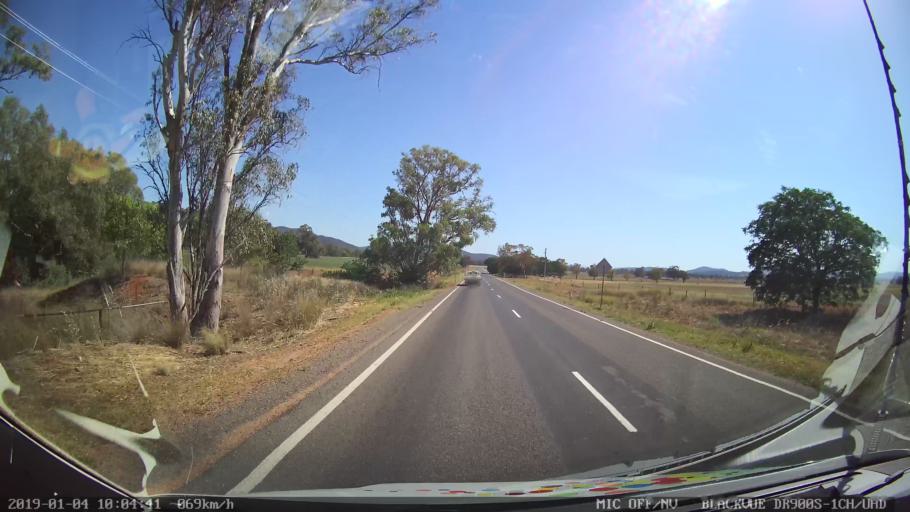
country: AU
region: New South Wales
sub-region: Cabonne
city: Canowindra
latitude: -33.4499
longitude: 148.3621
